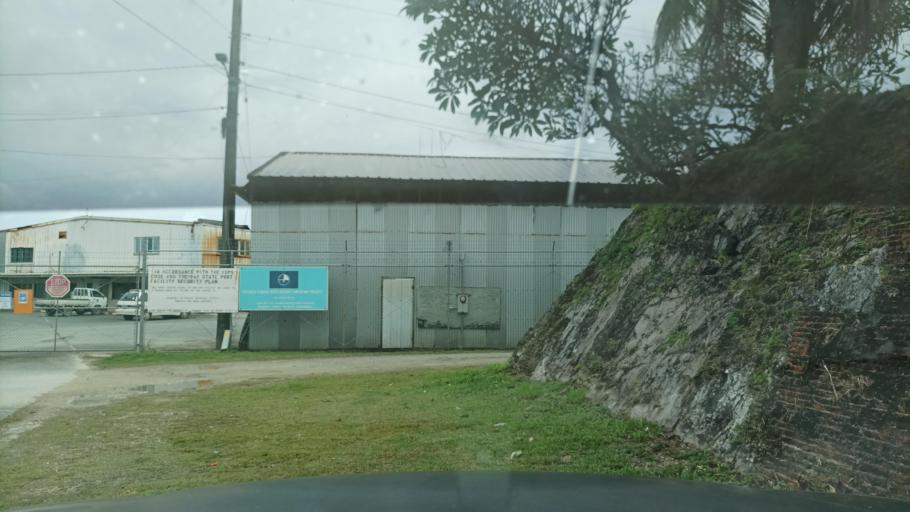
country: FM
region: Yap
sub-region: Weloy Municipality
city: Colonia
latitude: 9.5158
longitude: 138.1241
